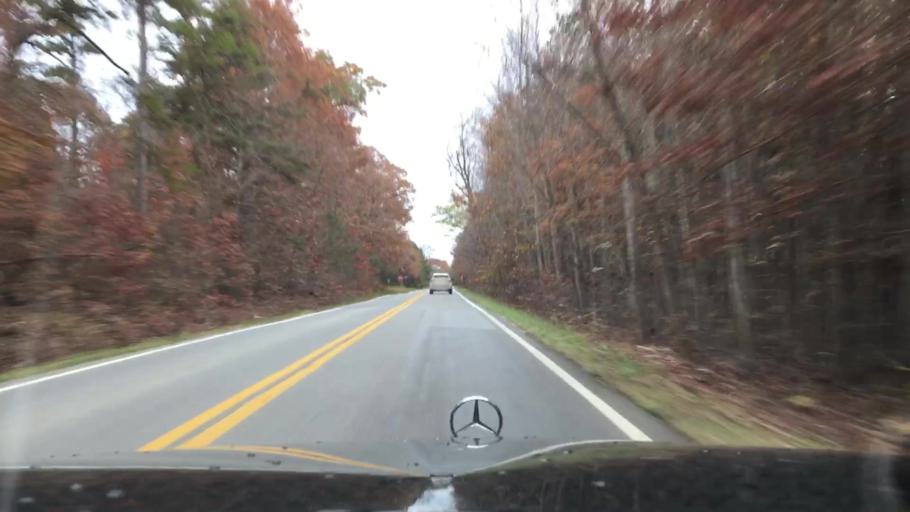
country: US
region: Virginia
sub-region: Campbell County
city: Timberlake
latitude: 37.2475
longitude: -79.2816
